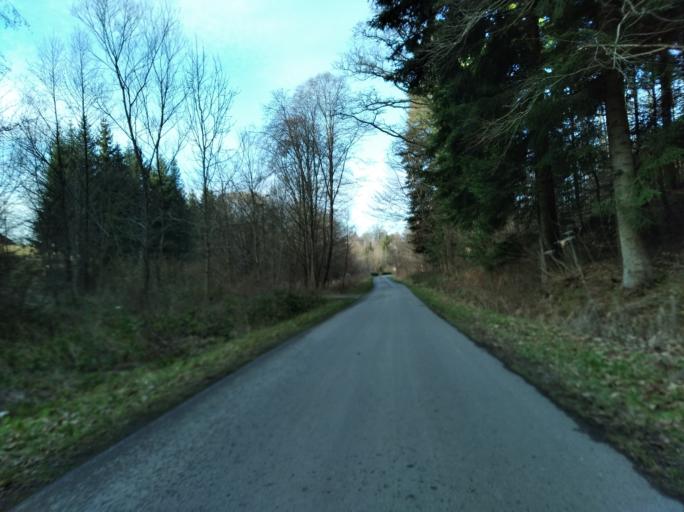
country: PL
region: Subcarpathian Voivodeship
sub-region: Powiat strzyzowski
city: Konieczkowa
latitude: 49.8281
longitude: 21.9398
